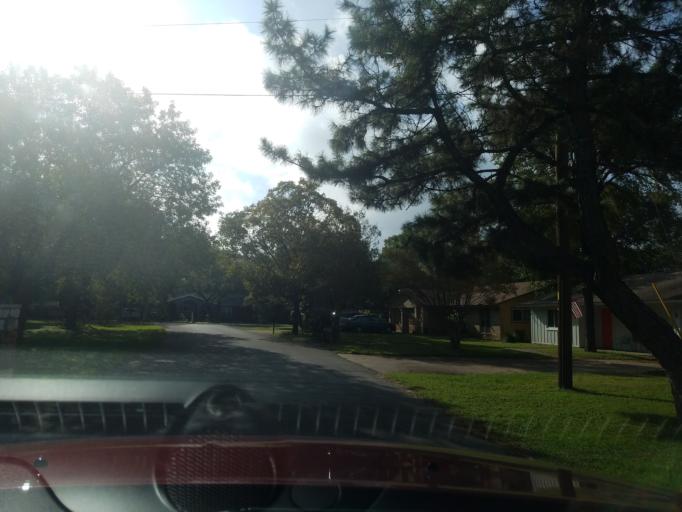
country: US
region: Texas
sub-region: Williamson County
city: Jollyville
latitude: 30.4531
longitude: -97.7828
